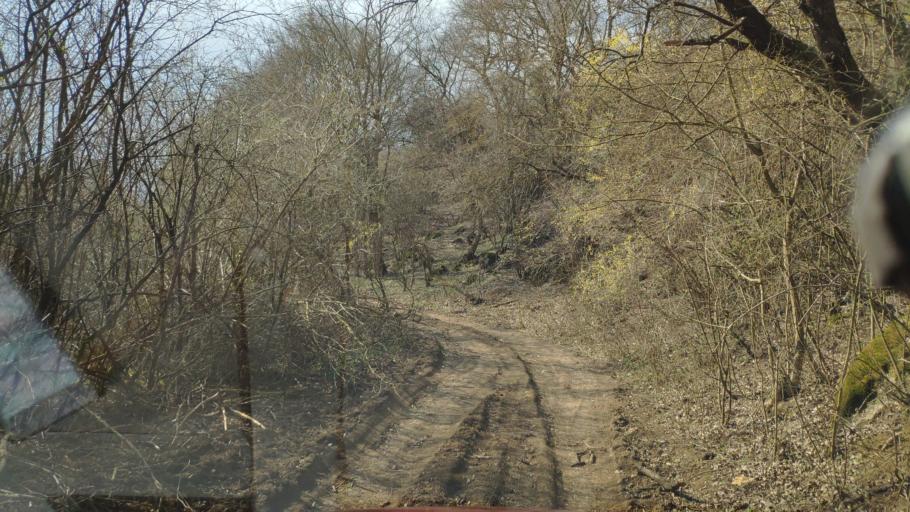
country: SK
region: Kosicky
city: Moldava nad Bodvou
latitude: 48.6170
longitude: 20.9152
